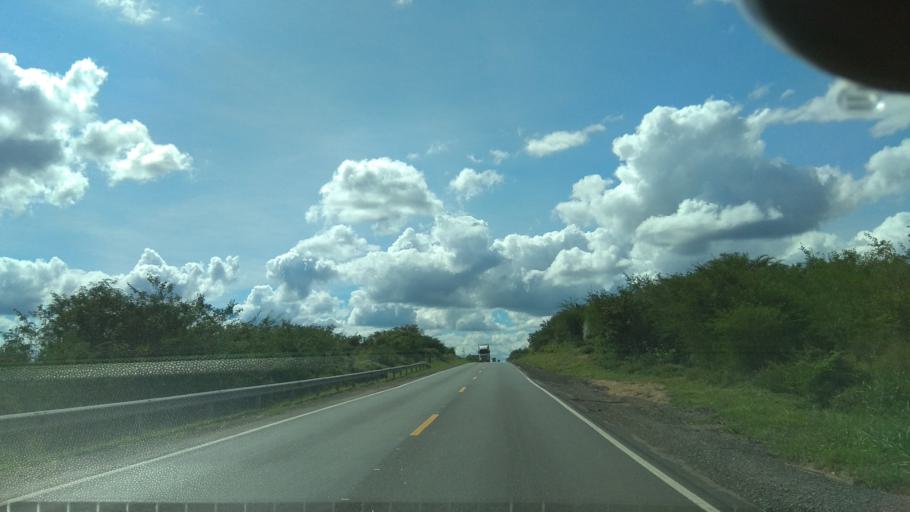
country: BR
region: Bahia
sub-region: Jaguaquara
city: Jaguaquara
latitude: -13.4376
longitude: -40.0295
